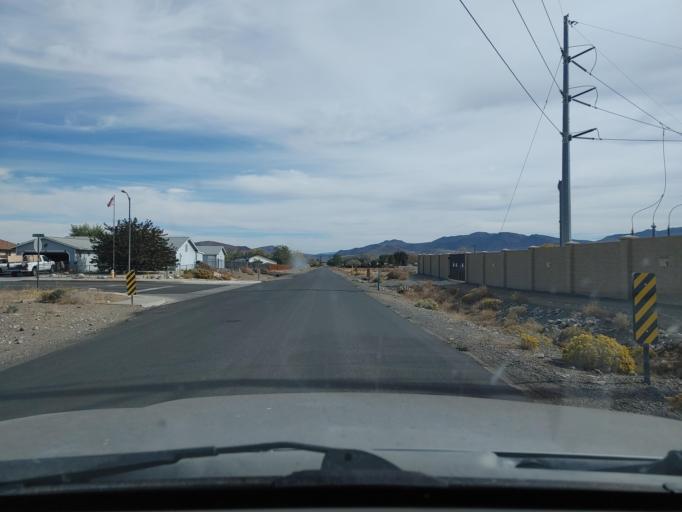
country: US
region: Nevada
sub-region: Lyon County
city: Dayton
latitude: 39.3034
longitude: -119.5463
